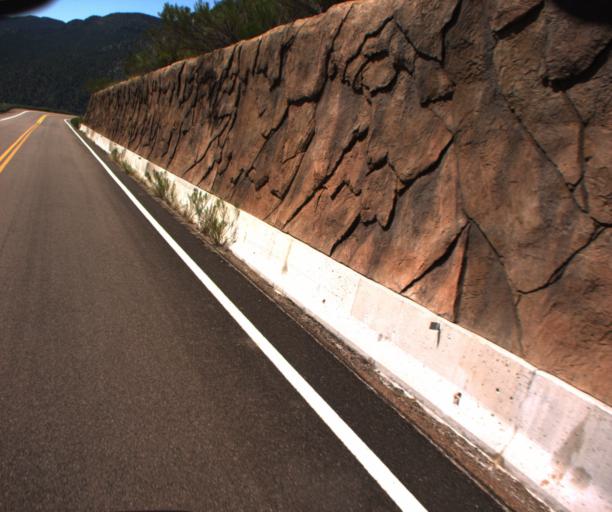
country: US
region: Arizona
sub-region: Navajo County
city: Cibecue
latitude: 33.8045
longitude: -110.4861
